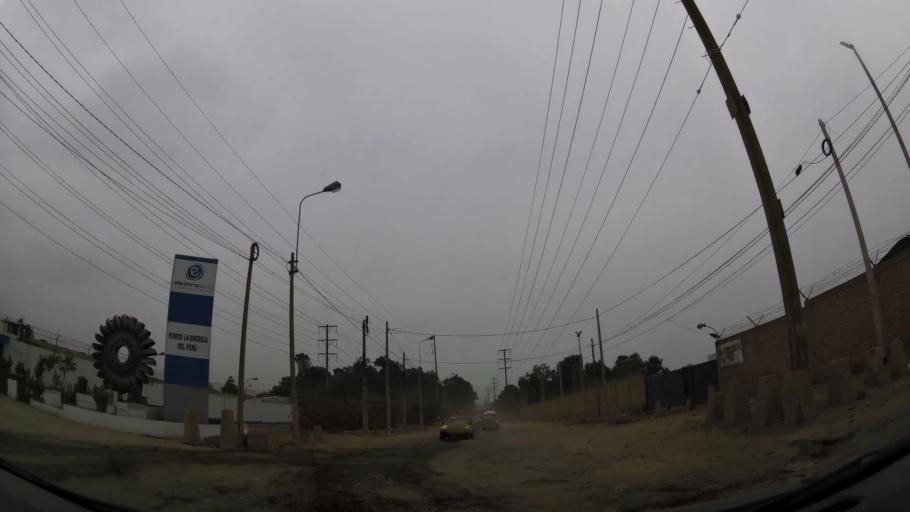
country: PE
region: Lima
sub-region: Lima
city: Surco
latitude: -12.1795
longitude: -76.9750
